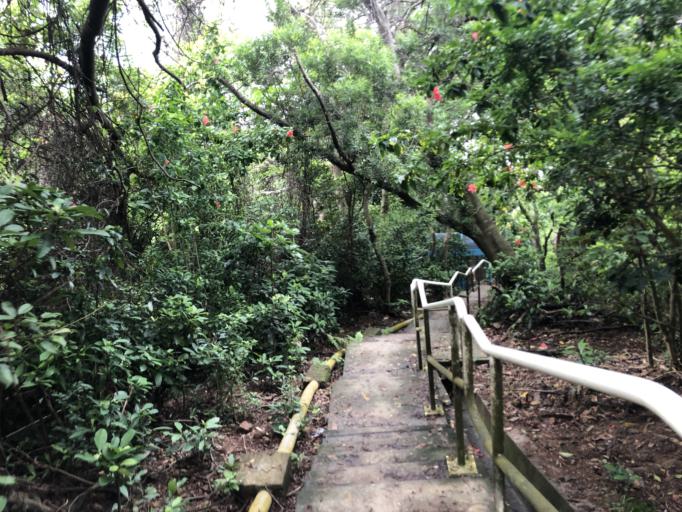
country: HK
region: Wanchai
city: Wan Chai
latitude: 22.2640
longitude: 114.2437
